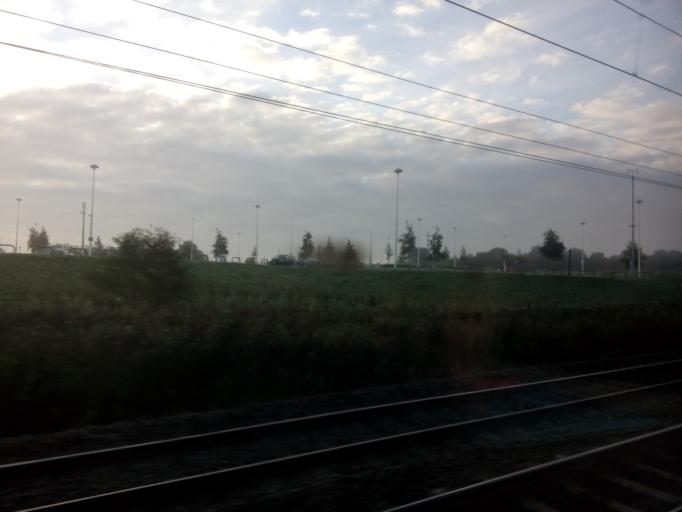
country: GB
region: England
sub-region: City of York
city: Bishopthorpe
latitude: 53.9294
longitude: -1.1199
